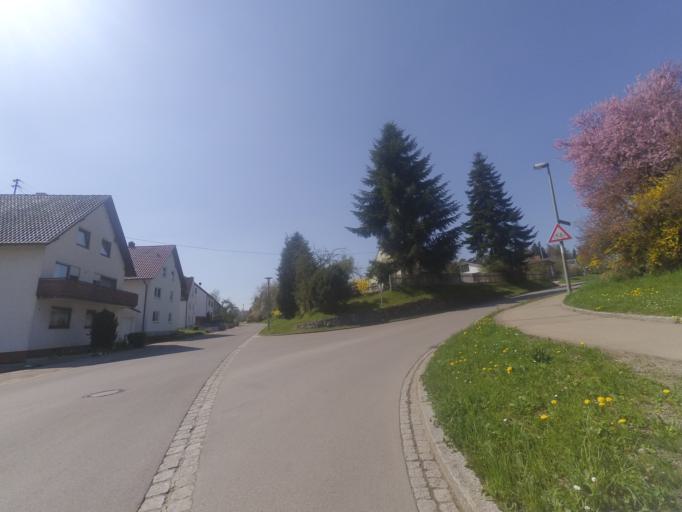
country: DE
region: Bavaria
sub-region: Swabia
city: Roggenburg
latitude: 48.3133
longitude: 10.2115
